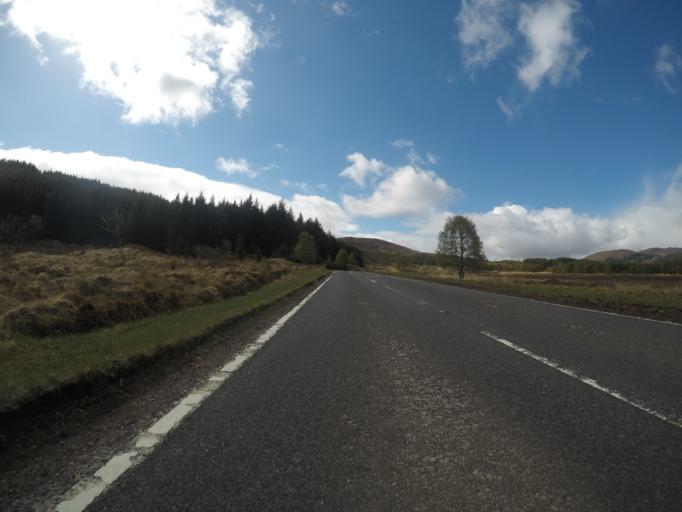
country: GB
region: Scotland
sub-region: Highland
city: Spean Bridge
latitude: 57.1295
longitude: -4.9623
